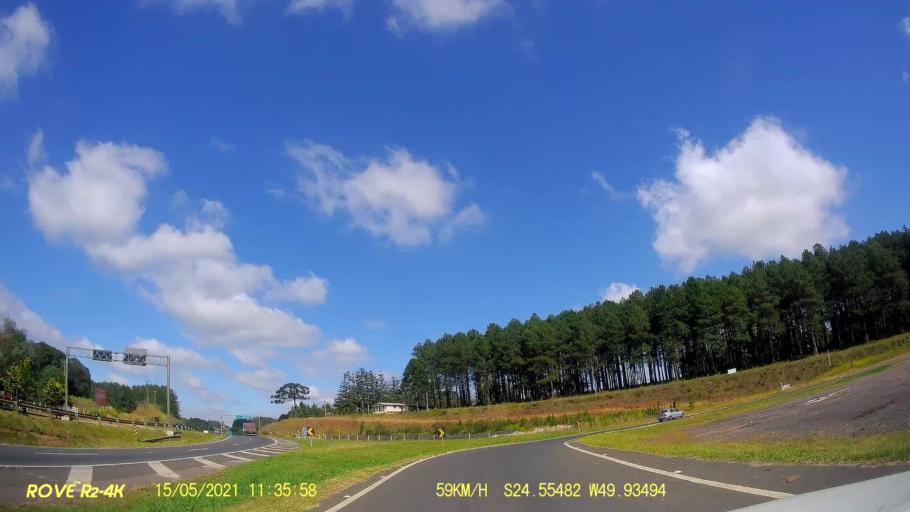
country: BR
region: Parana
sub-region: Pirai Do Sul
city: Pirai do Sul
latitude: -24.5545
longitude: -49.9348
